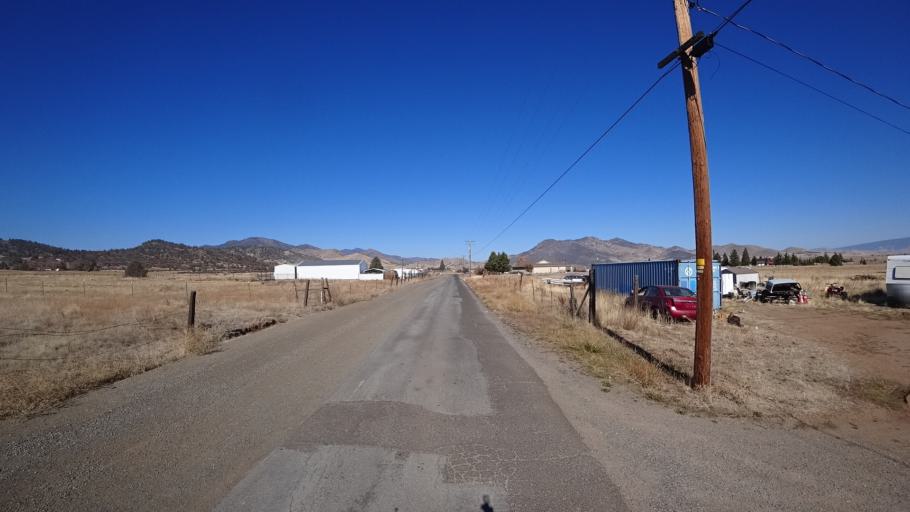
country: US
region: California
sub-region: Siskiyou County
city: Yreka
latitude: 41.7405
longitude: -122.5932
